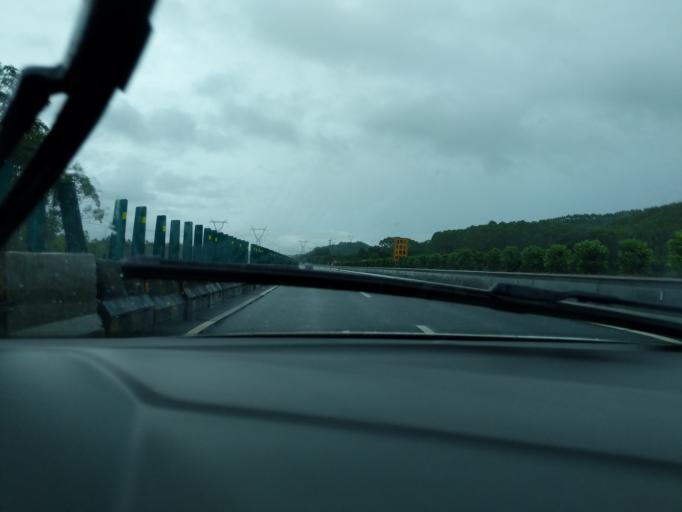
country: CN
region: Guangdong
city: Liangxi
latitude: 22.2750
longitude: 112.3320
